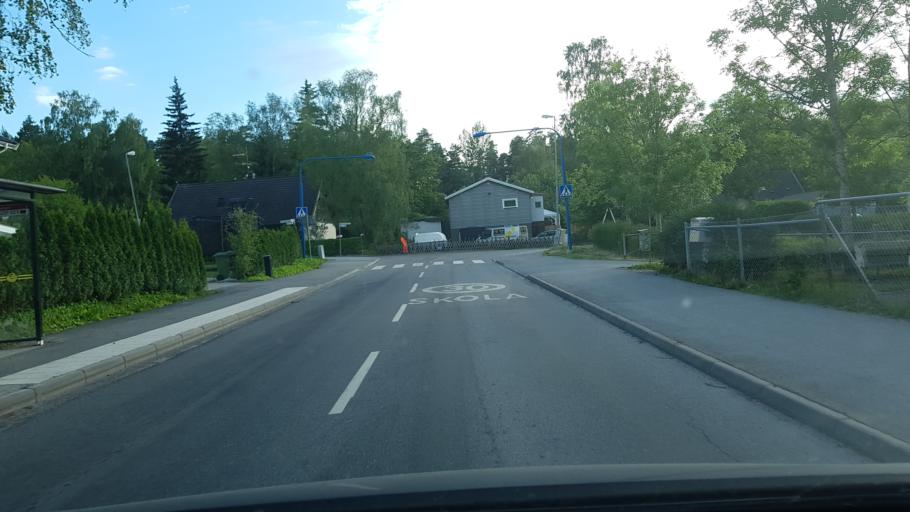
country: SE
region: Stockholm
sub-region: Sollentuna Kommun
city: Sollentuna
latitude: 59.4559
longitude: 17.8949
